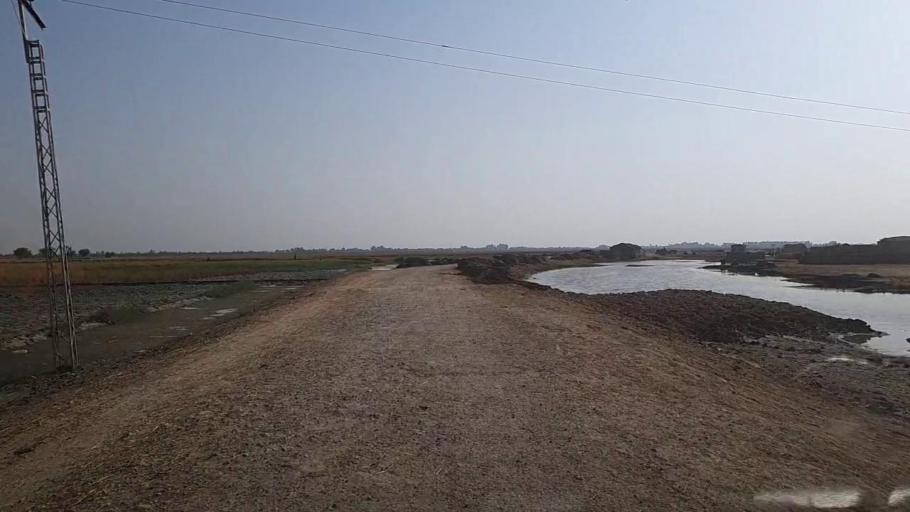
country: PK
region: Sindh
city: Kandhkot
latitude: 28.3699
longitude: 69.3330
